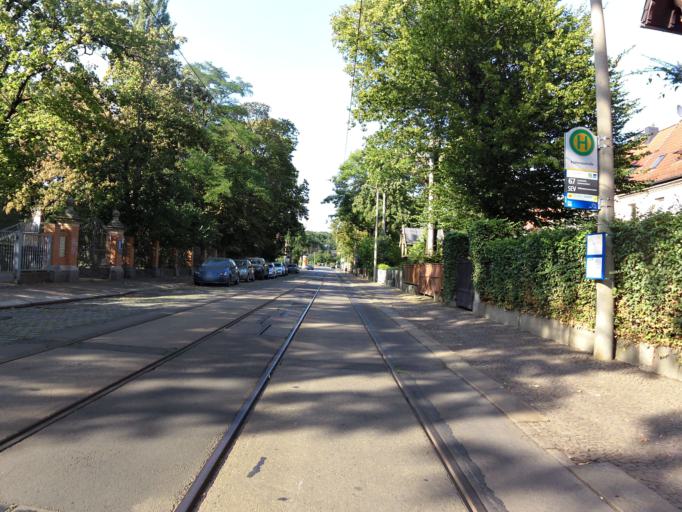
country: DE
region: Saxony
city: Leipzig
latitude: 51.3549
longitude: 12.3152
